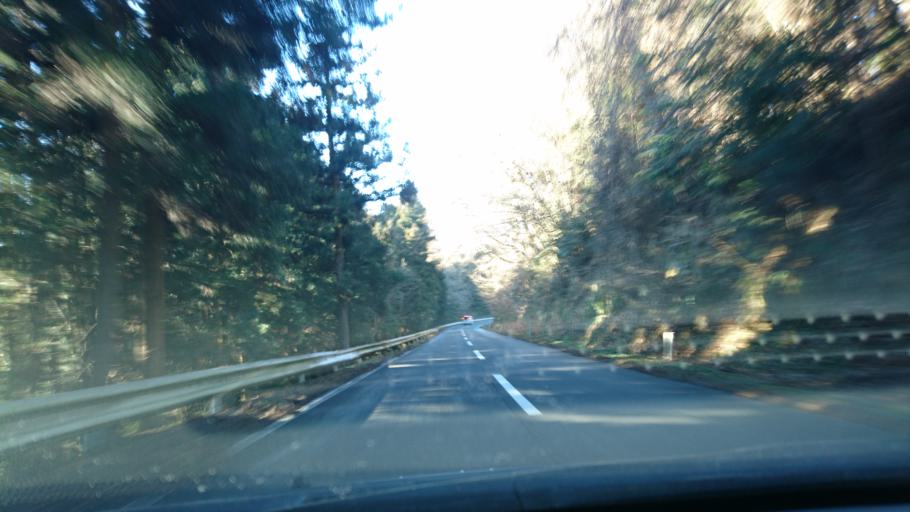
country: JP
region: Iwate
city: Ichinoseki
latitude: 38.8535
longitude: 141.2980
